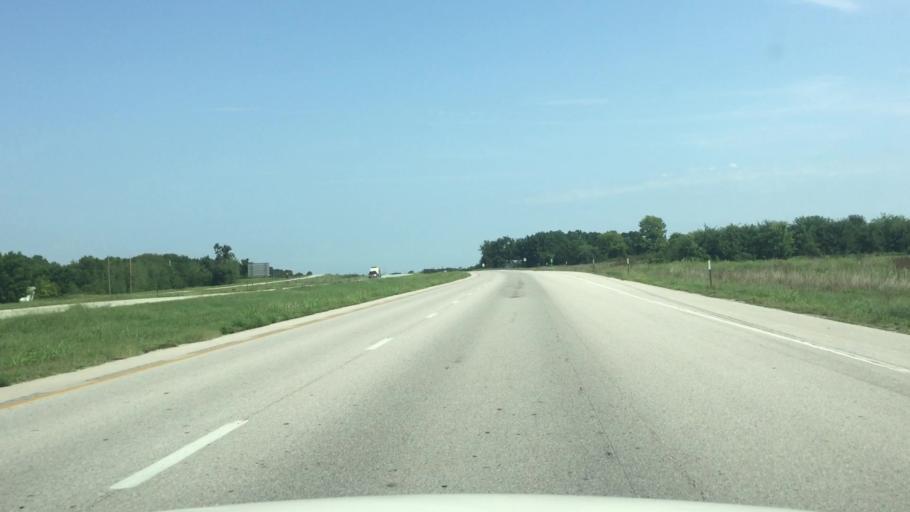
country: US
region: Kansas
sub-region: Montgomery County
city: Coffeyville
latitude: 37.0513
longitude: -95.5810
